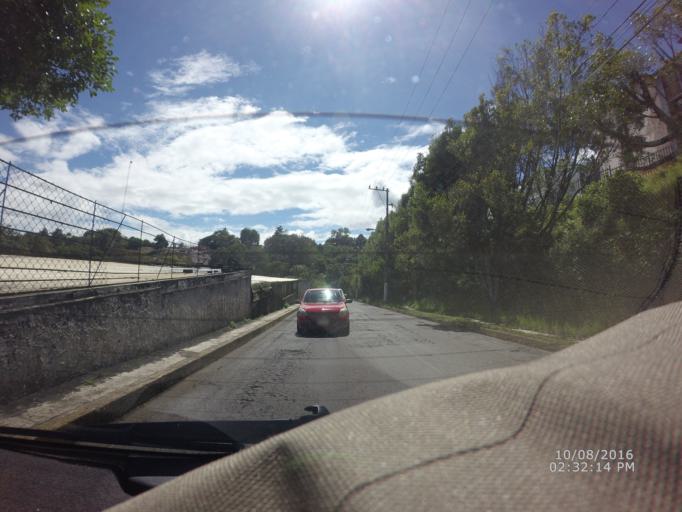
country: MX
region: Veracruz
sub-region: Xalapa
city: Lomas Verdes
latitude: 19.5130
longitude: -96.9053
